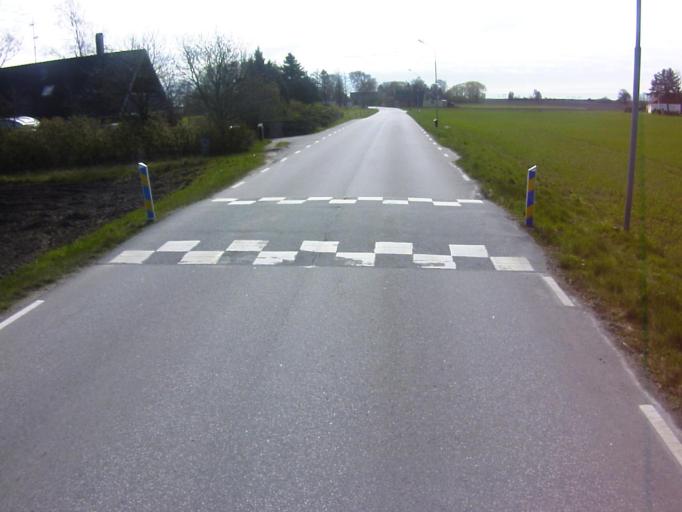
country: SE
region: Skane
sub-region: Kavlinge Kommun
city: Hofterup
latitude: 55.7895
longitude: 12.9704
